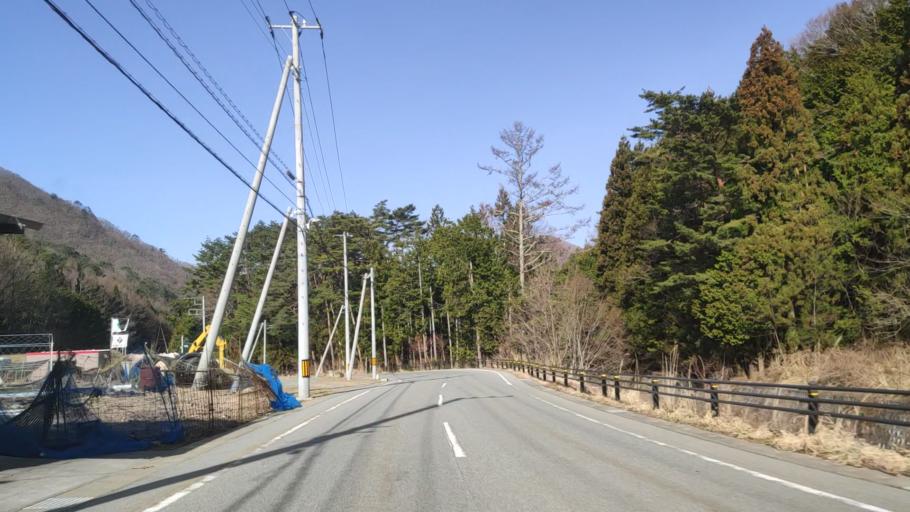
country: JP
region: Yamanashi
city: Fujikawaguchiko
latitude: 35.5533
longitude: 138.6845
